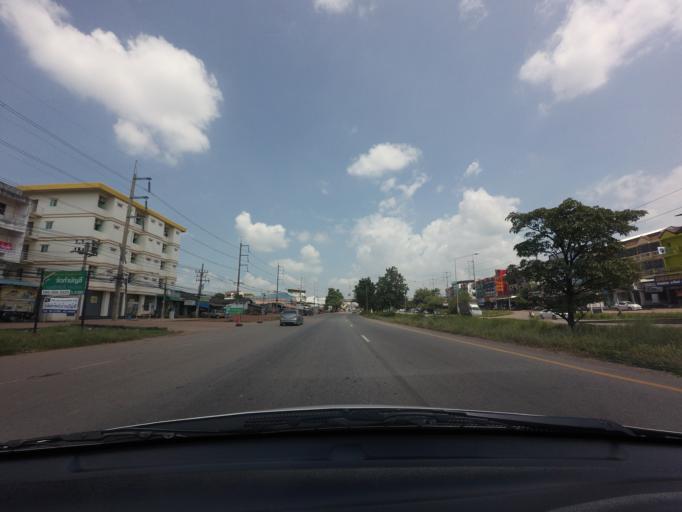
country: TH
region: Prachin Buri
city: Si Maha Phot
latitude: 13.8963
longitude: 101.5836
